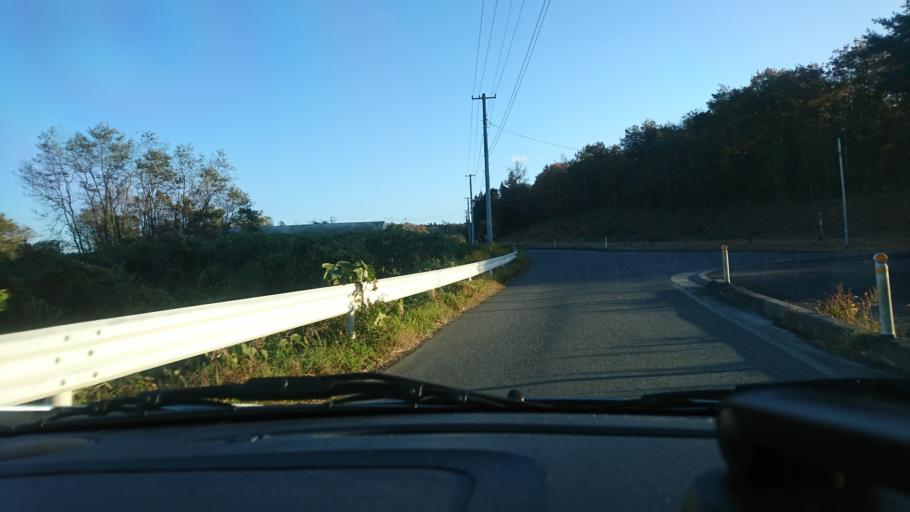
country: JP
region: Iwate
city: Ichinoseki
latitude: 38.7863
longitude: 141.2320
